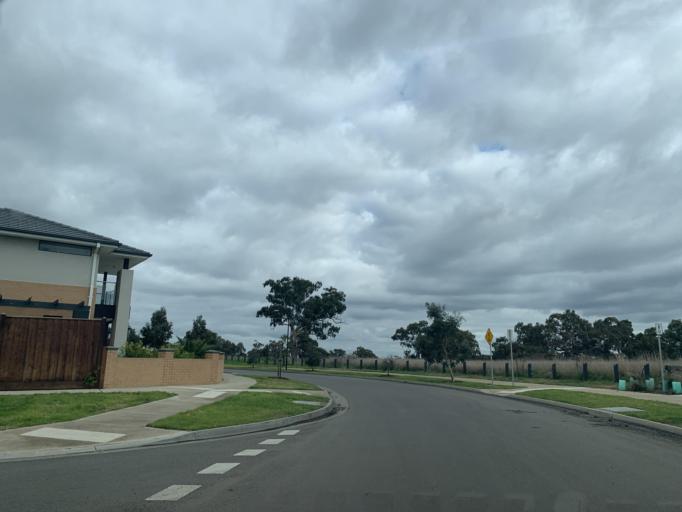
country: AU
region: Victoria
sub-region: Hume
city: Craigieburn
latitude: -37.6013
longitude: 144.9965
